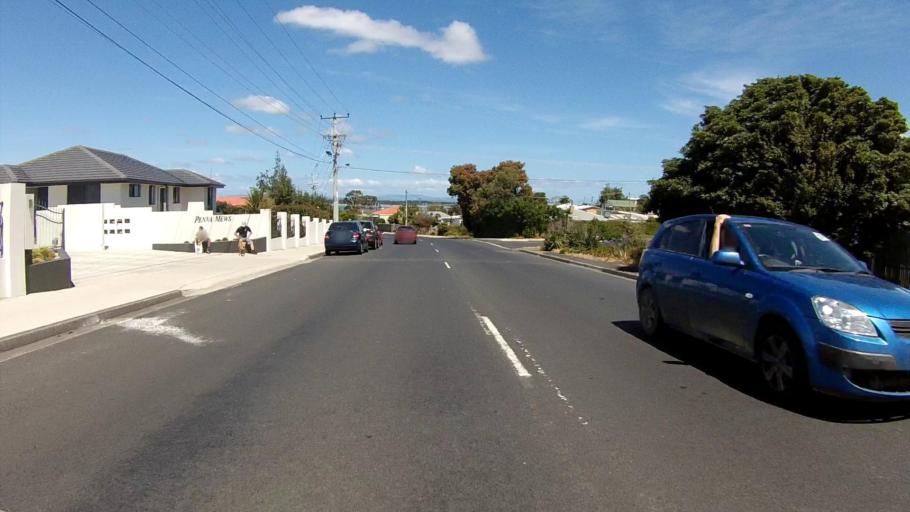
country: AU
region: Tasmania
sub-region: Sorell
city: Sorell
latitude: -42.8012
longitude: 147.5297
